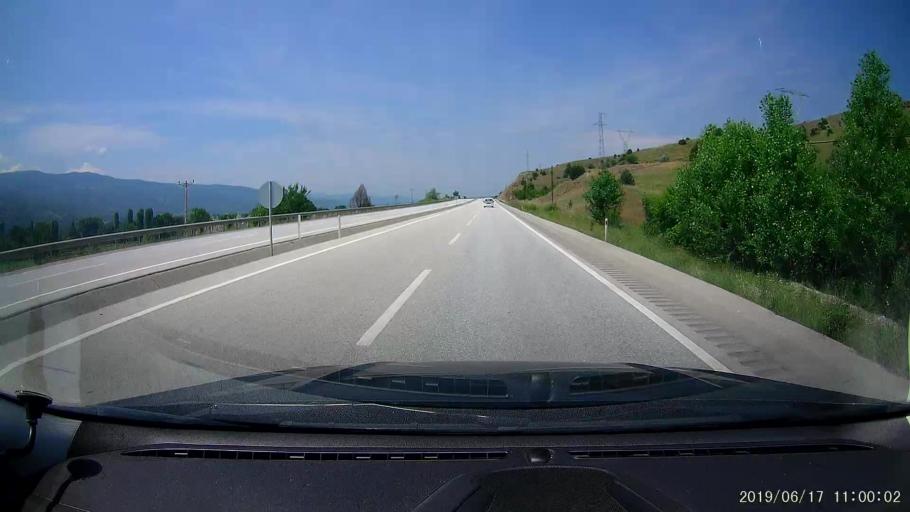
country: TR
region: Kastamonu
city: Tosya
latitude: 41.0380
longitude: 34.1913
